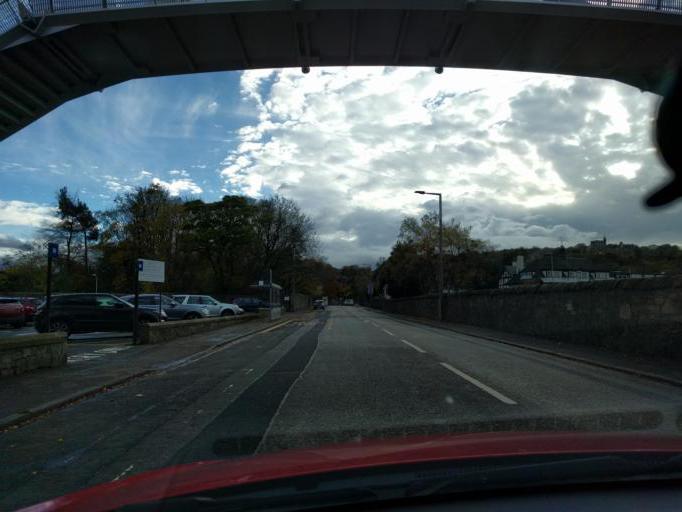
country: GB
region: Scotland
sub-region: Edinburgh
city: Edinburgh
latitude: 55.9277
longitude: -3.2238
